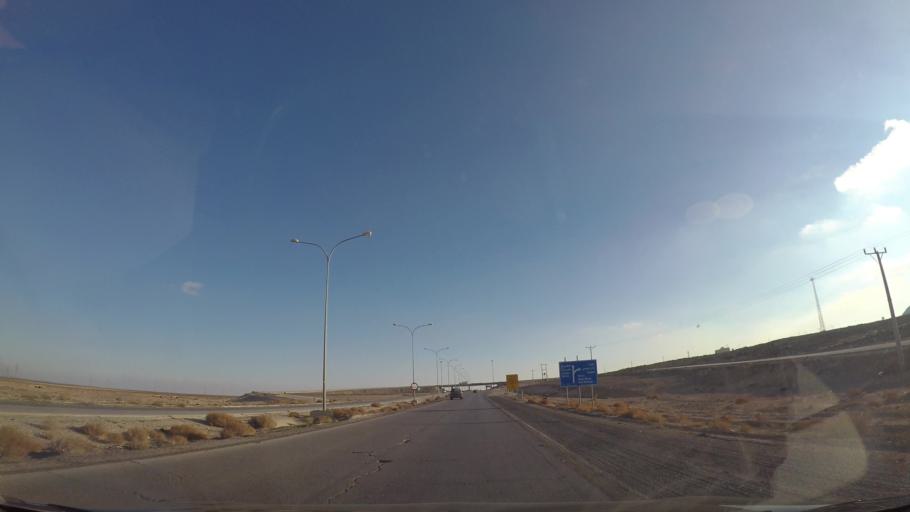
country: JO
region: Tafielah
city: Busayra
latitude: 30.5024
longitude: 35.7995
